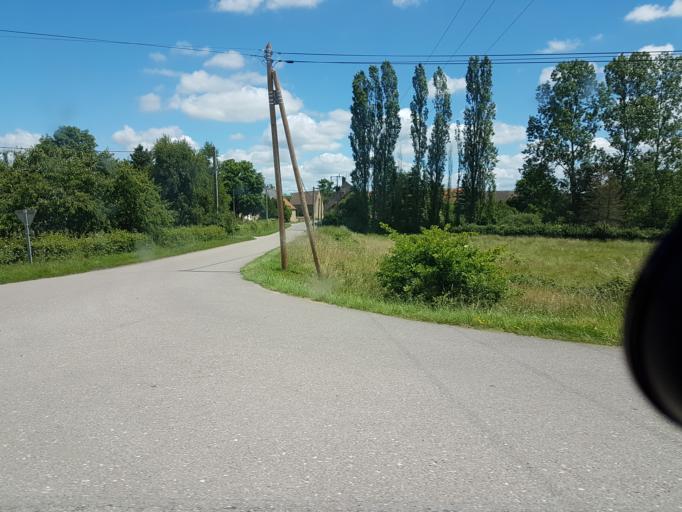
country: FR
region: Bourgogne
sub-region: Departement de Saone-et-Loire
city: Curgy
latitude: 47.0337
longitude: 4.4115
